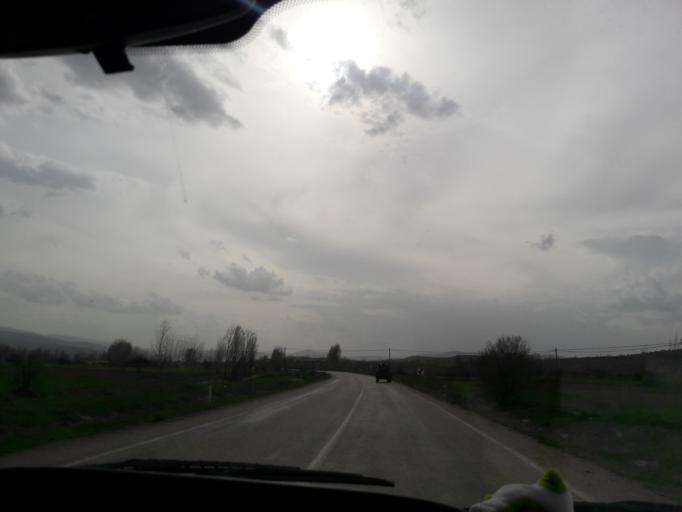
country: TR
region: Gumushane
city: Siran
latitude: 40.1774
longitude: 39.0969
